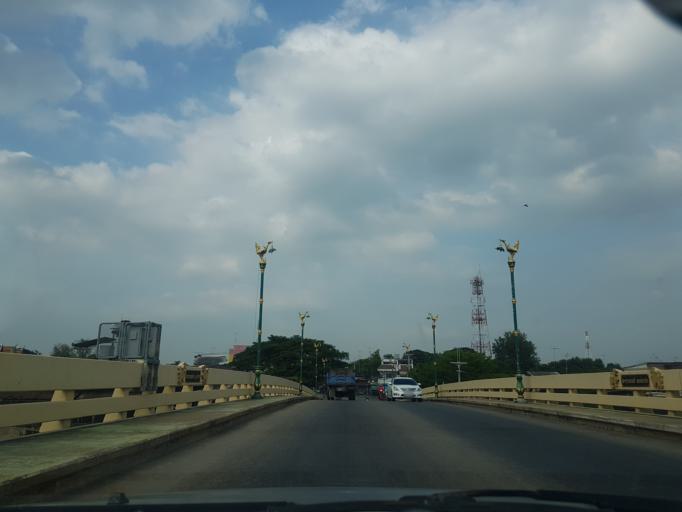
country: TH
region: Phra Nakhon Si Ayutthaya
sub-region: Amphoe Tha Ruea
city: Tha Ruea
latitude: 14.5601
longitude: 100.7198
